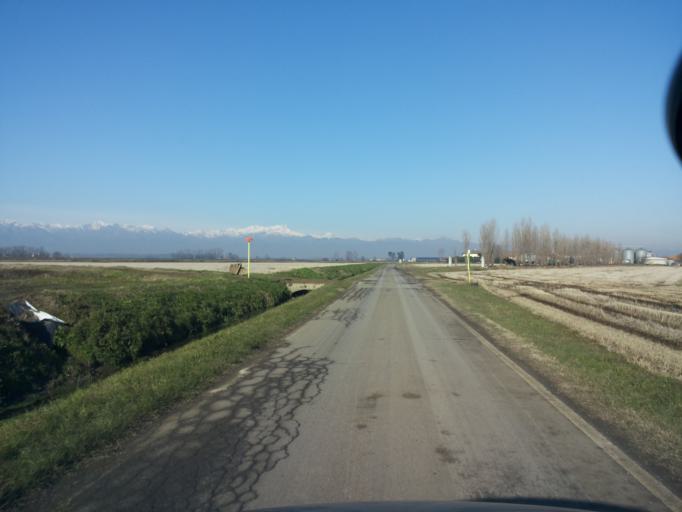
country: IT
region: Piedmont
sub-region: Provincia di Vercelli
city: San Germano Vercellese
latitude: 45.3660
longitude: 8.2419
